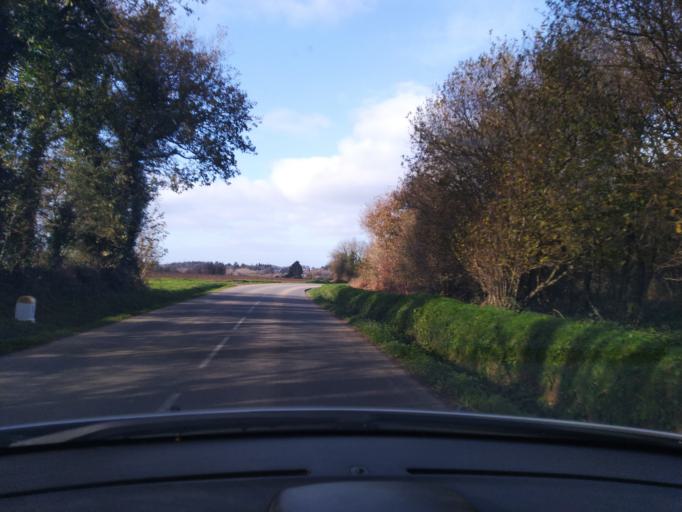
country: FR
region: Brittany
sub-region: Departement du Finistere
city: Plouigneau
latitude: 48.5546
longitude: -3.6891
